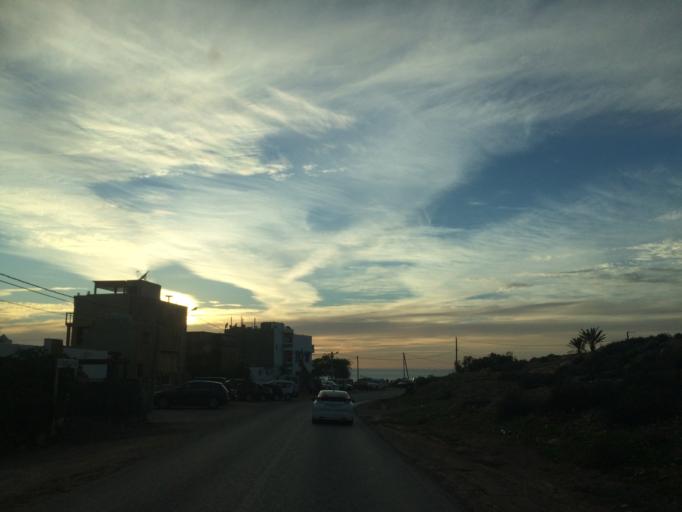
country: MA
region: Souss-Massa-Draa
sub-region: Agadir-Ida-ou-Tnan
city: Taghazout
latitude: 30.5466
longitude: -9.7238
